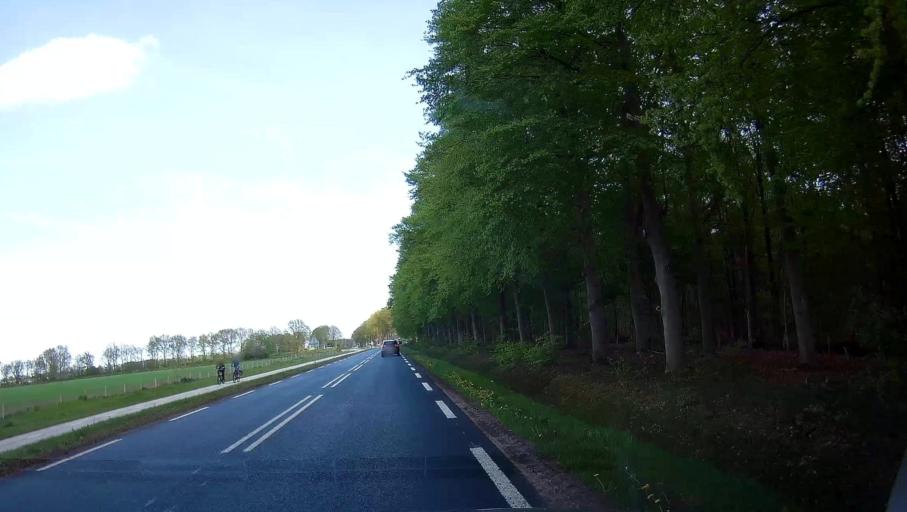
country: NL
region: Drenthe
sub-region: Gemeente Borger-Odoorn
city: Borger
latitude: 52.9094
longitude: 6.7241
